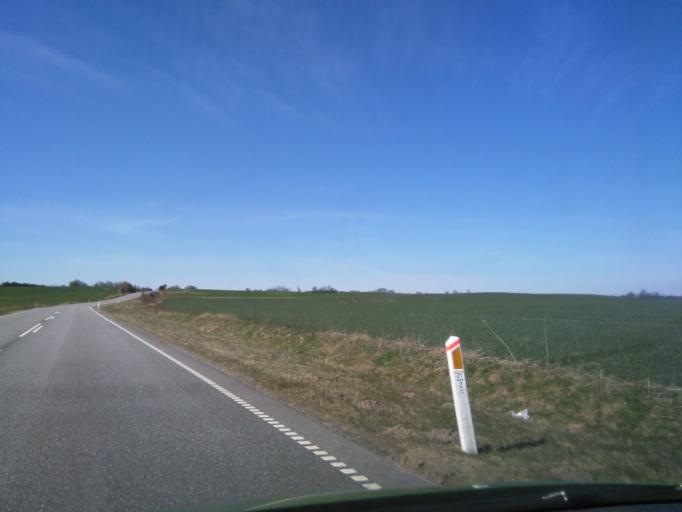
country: DK
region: Central Jutland
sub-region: Horsens Kommune
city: Braedstrup
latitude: 56.0218
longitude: 9.6254
